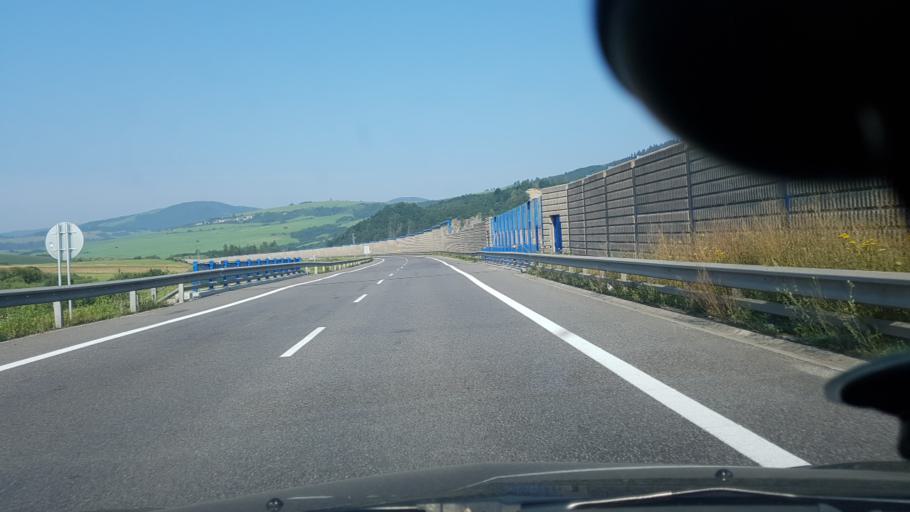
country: SK
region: Zilinsky
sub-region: Okres Zilina
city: Trstena
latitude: 49.3520
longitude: 19.6039
